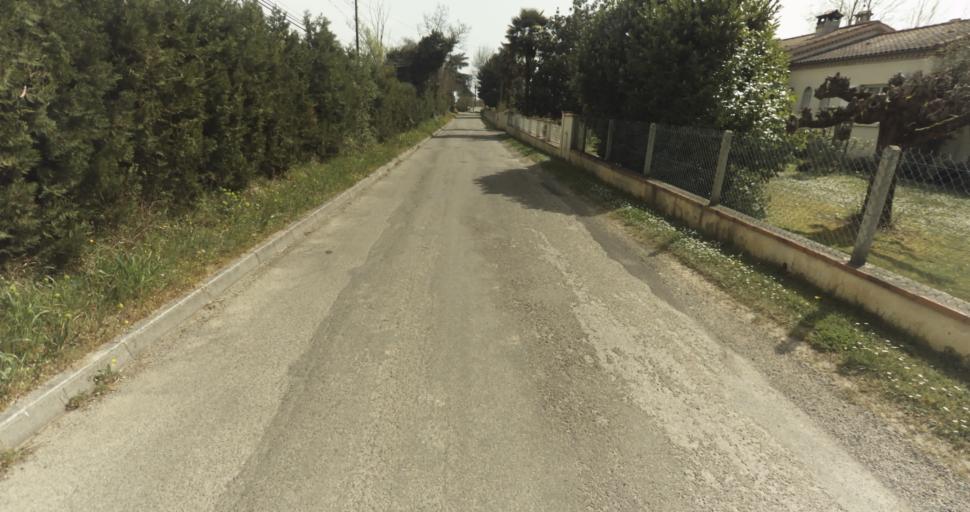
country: FR
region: Midi-Pyrenees
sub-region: Departement du Tarn-et-Garonne
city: Moissac
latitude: 44.1194
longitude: 1.1072
